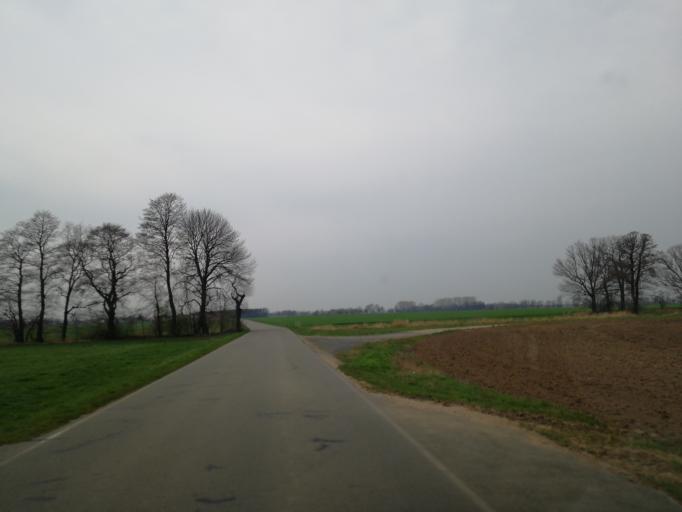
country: DE
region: Brandenburg
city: Elsterwerda
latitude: 51.4407
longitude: 13.4728
